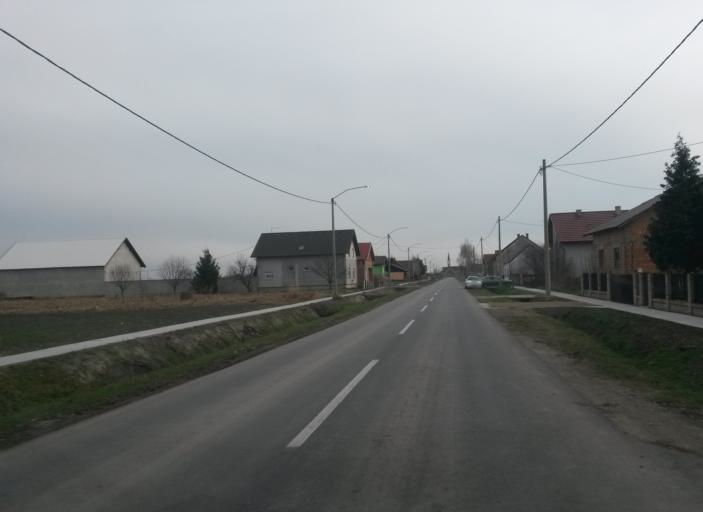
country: HR
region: Osjecko-Baranjska
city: Antunovac
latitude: 45.4911
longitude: 18.6267
